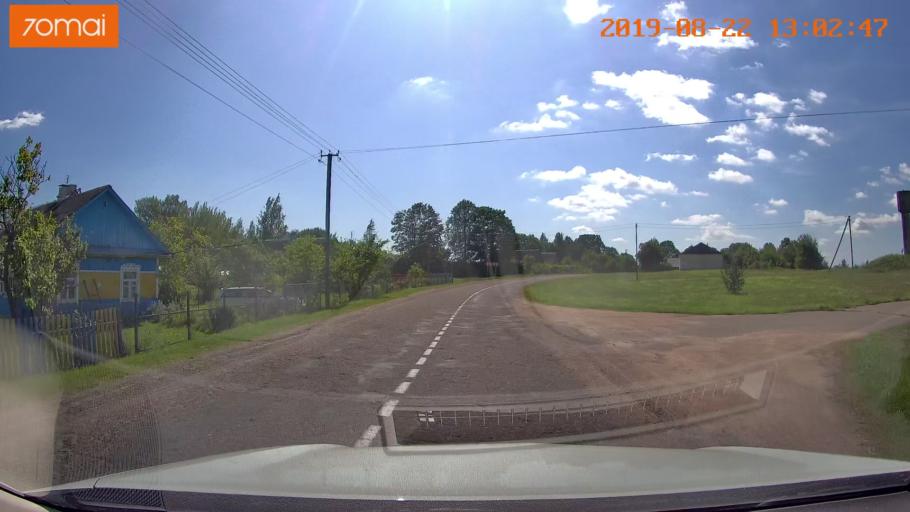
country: BY
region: Minsk
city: Prawdzinski
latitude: 53.3856
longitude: 27.8251
